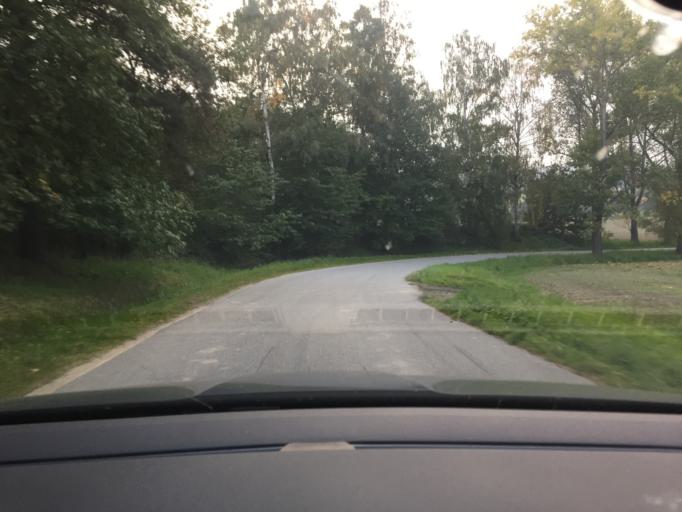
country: CZ
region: Jihocesky
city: Brloh
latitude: 48.9740
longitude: 14.2709
